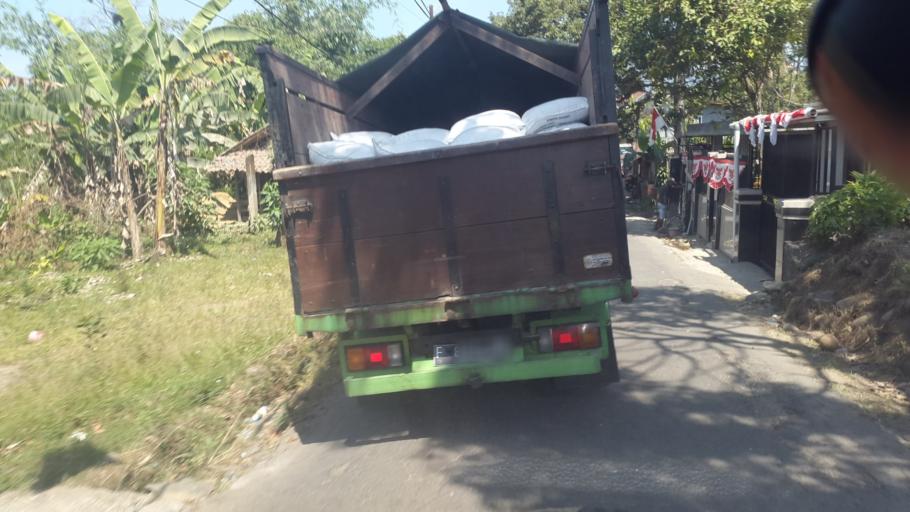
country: ID
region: Banten
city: Kubang
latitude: -6.7905
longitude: 106.6195
